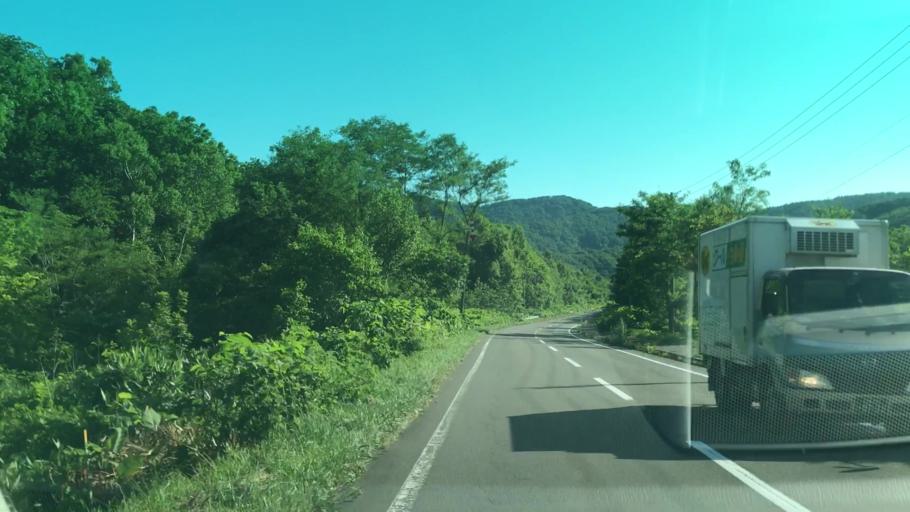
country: JP
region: Hokkaido
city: Yoichi
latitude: 43.0721
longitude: 140.7101
